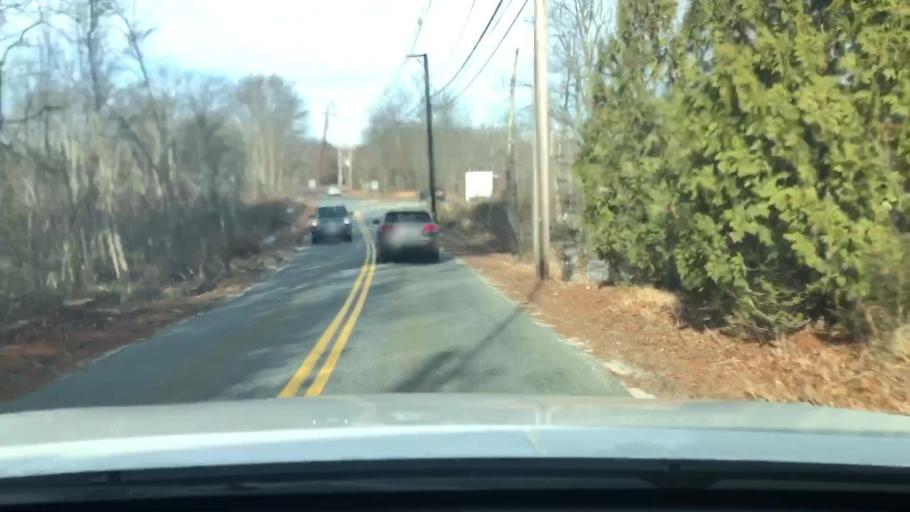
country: US
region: Massachusetts
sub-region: Worcester County
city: Milford
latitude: 42.1406
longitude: -71.4876
